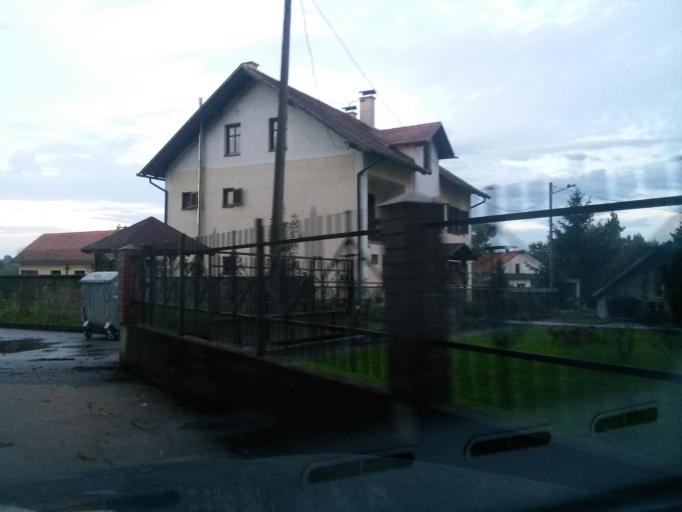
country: HR
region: Sisacko-Moslavacka
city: Gvozd
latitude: 45.2962
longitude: 15.9783
